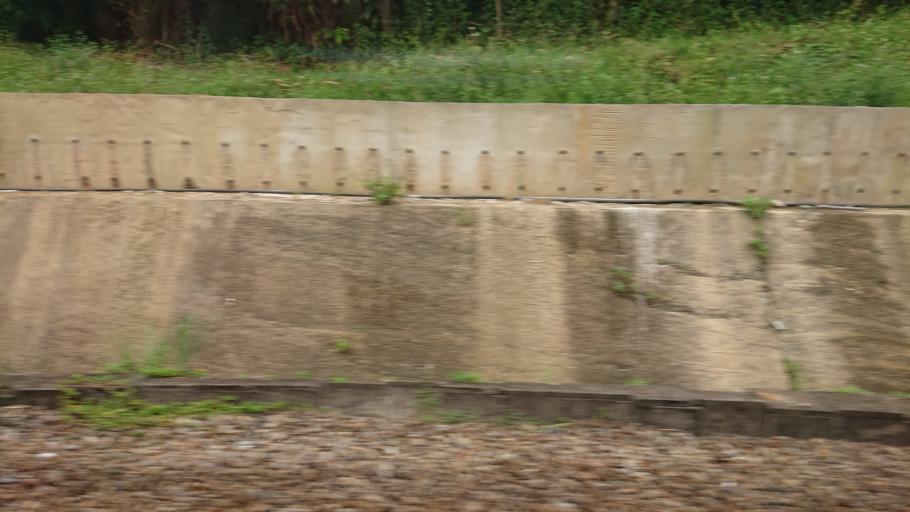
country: TW
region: Taiwan
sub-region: Keelung
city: Keelung
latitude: 24.9617
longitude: 121.9199
